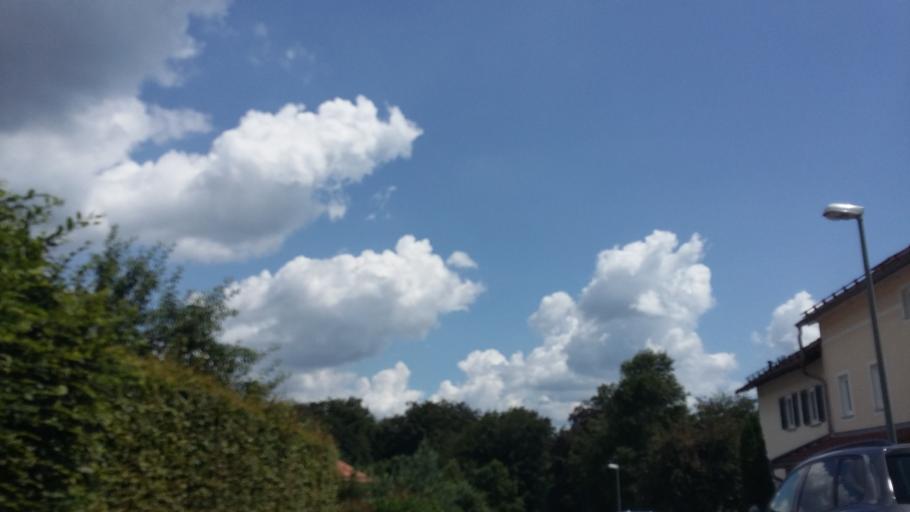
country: DE
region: Bavaria
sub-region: Upper Bavaria
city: Starnberg
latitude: 48.0123
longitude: 11.3429
